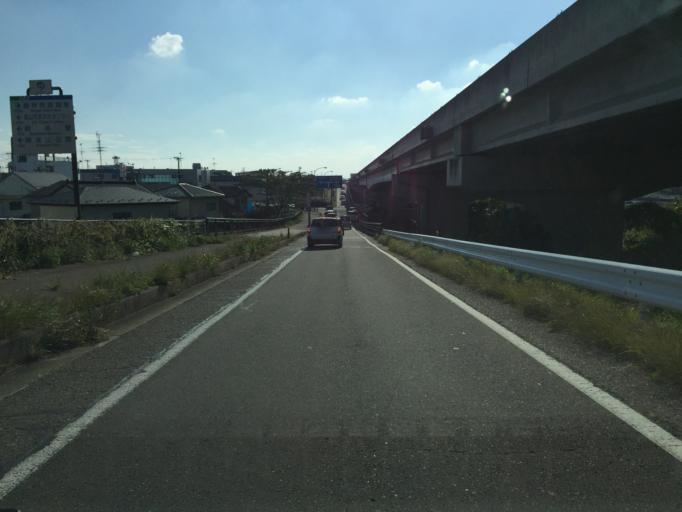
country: JP
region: Fukushima
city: Koriyama
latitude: 37.4132
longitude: 140.3480
